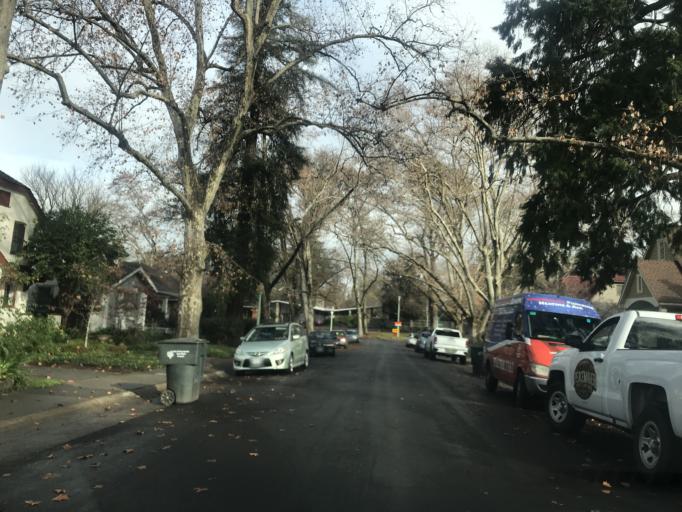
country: US
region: California
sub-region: Sacramento County
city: Sacramento
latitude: 38.5754
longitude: -121.4590
